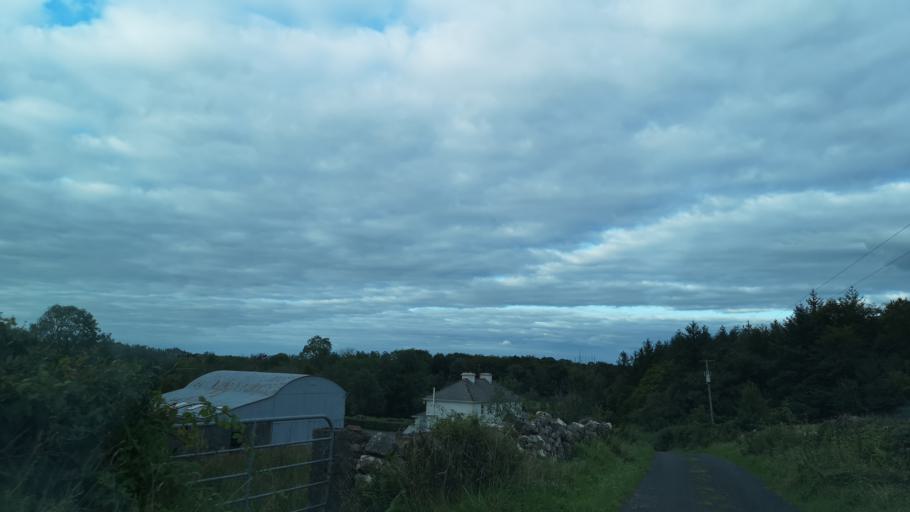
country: IE
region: Connaught
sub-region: County Galway
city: Loughrea
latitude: 53.1446
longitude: -8.5185
